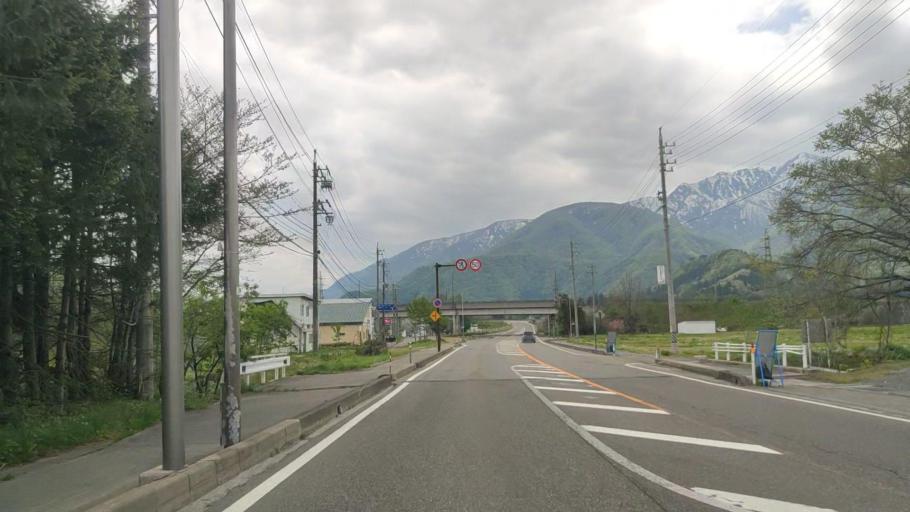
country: JP
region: Nagano
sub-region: Kitaazumi Gun
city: Hakuba
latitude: 36.6751
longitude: 137.8521
